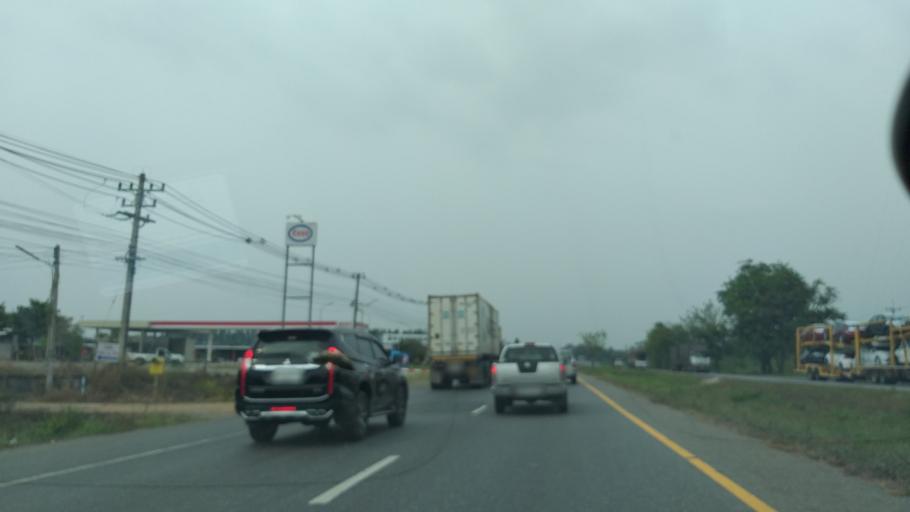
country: TH
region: Chon Buri
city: Ko Chan
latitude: 13.3156
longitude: 101.2672
